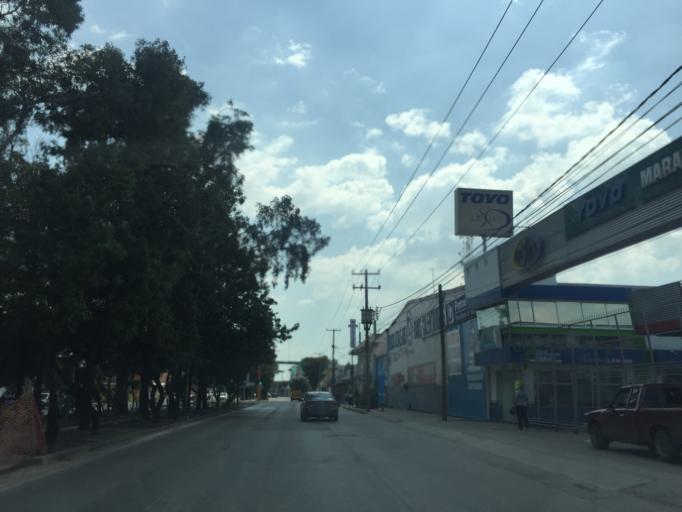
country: MX
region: Guanajuato
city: Leon
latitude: 21.1597
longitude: -101.6663
